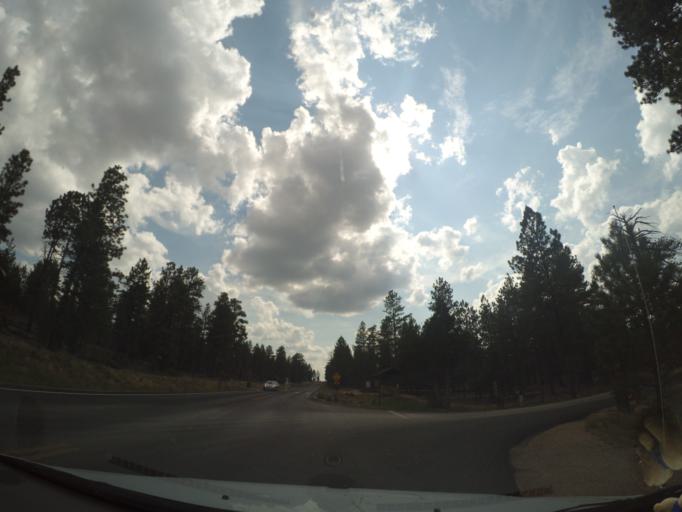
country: US
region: Utah
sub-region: Garfield County
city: Panguitch
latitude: 37.6225
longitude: -112.1718
